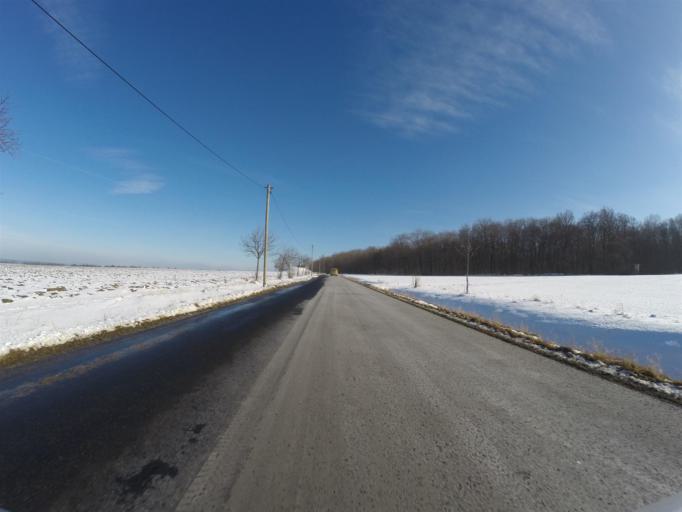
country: DE
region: Thuringia
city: Dobritschen
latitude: 50.9181
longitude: 11.4870
